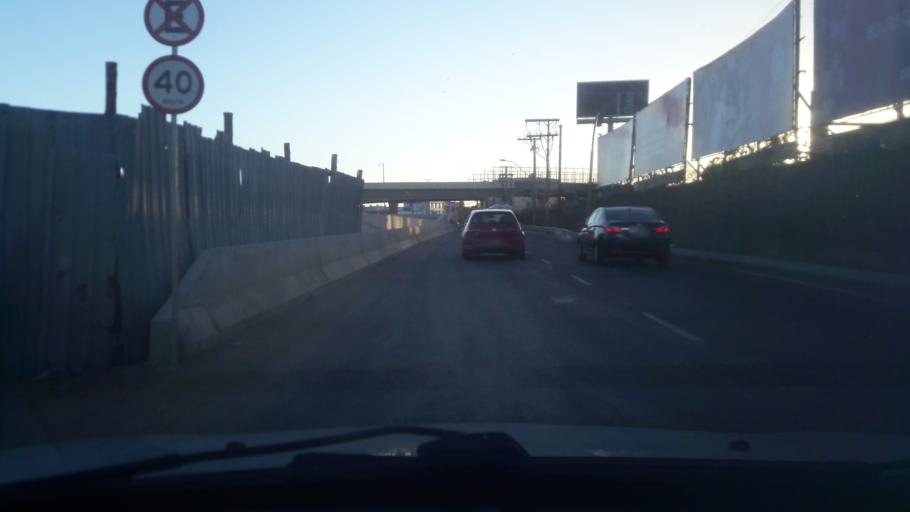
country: BR
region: Rio Grande do Sul
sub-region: Porto Alegre
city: Porto Alegre
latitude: -29.9950
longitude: -51.1885
